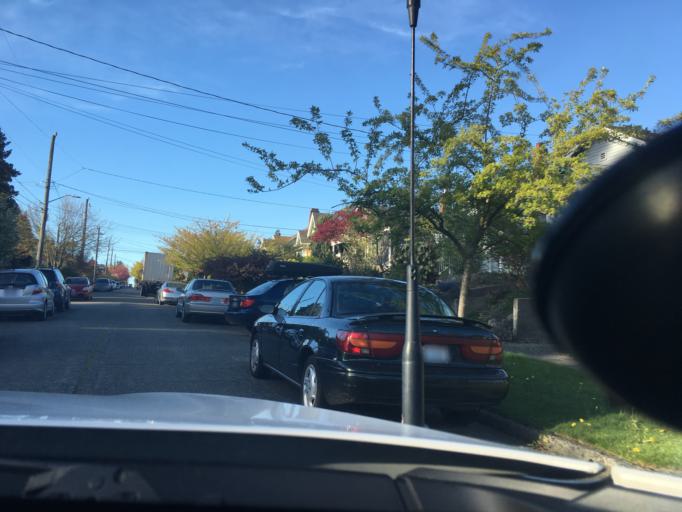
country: US
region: Washington
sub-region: King County
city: Shoreline
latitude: 47.6802
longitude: -122.3919
